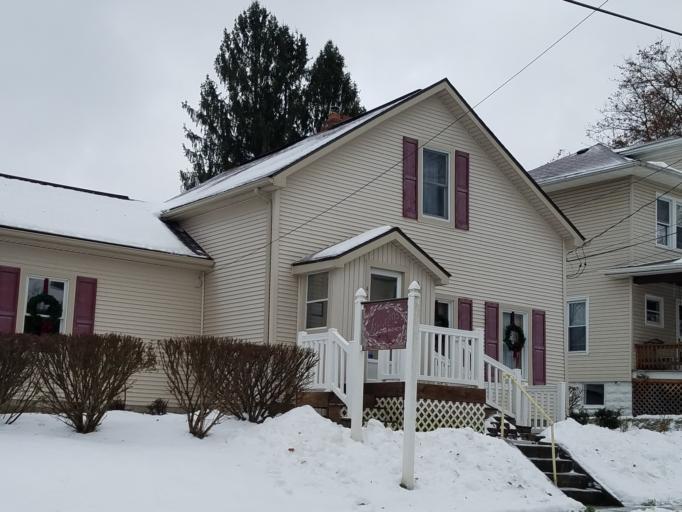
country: US
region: Pennsylvania
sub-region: Mercer County
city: Mercer
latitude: 41.2256
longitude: -80.2327
